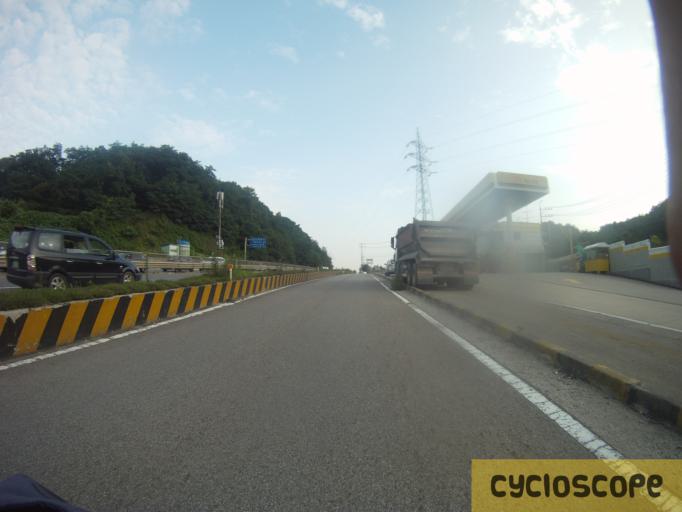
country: KR
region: Gyeonggi-do
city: Suwon-si
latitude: 37.2068
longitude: 126.9433
